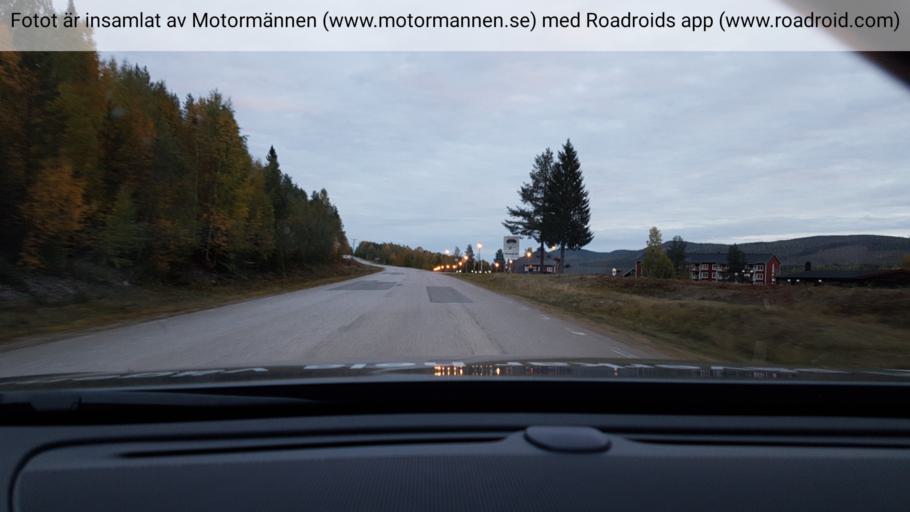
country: SE
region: Norrbotten
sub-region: Alvsbyns Kommun
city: AElvsbyn
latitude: 65.8590
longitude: 20.4200
